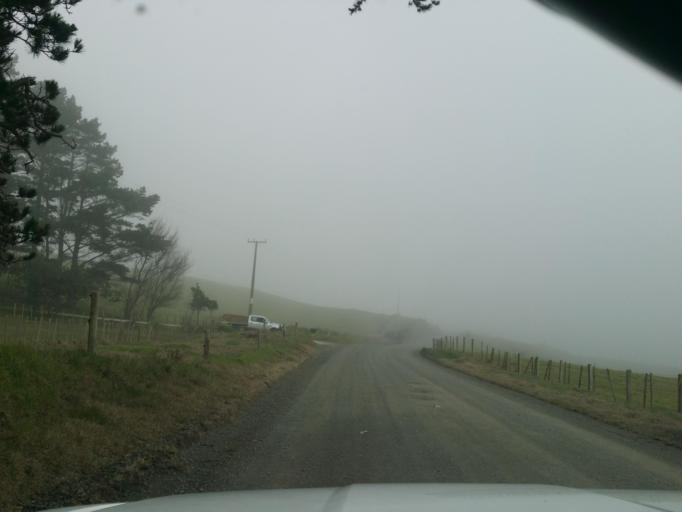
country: NZ
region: Northland
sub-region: Kaipara District
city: Dargaville
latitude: -35.9081
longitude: 173.7924
